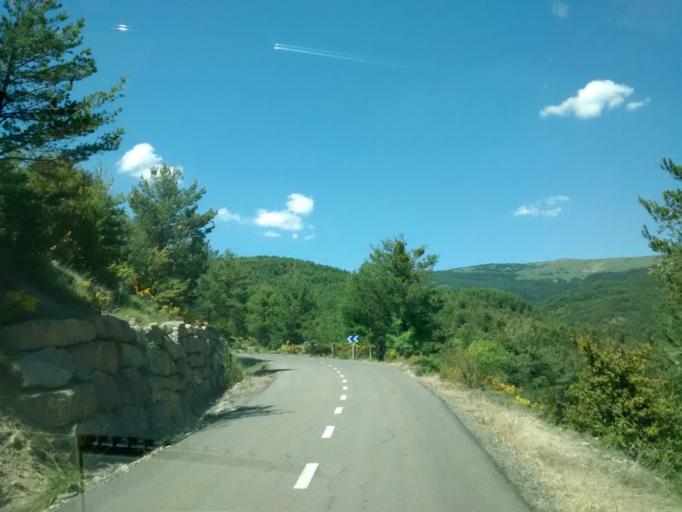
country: ES
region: Aragon
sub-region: Provincia de Huesca
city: Borau
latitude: 42.6688
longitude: -0.5939
